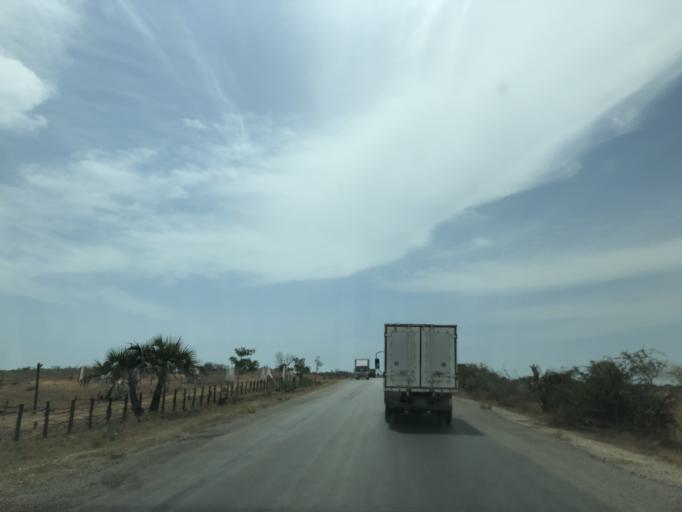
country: AO
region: Cuanza Sul
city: Sumbe
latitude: -10.5883
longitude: 13.7609
